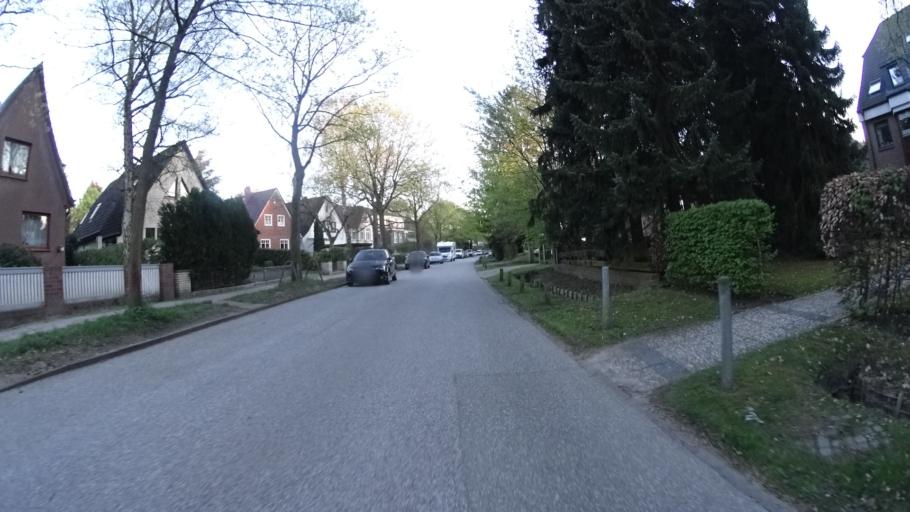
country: DE
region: Hamburg
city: Stellingen
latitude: 53.6274
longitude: 9.9558
